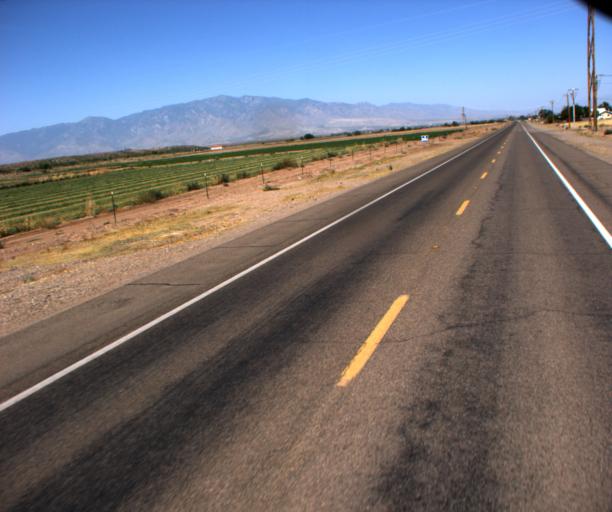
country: US
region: Arizona
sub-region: Graham County
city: Safford
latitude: 32.8128
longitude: -109.6037
